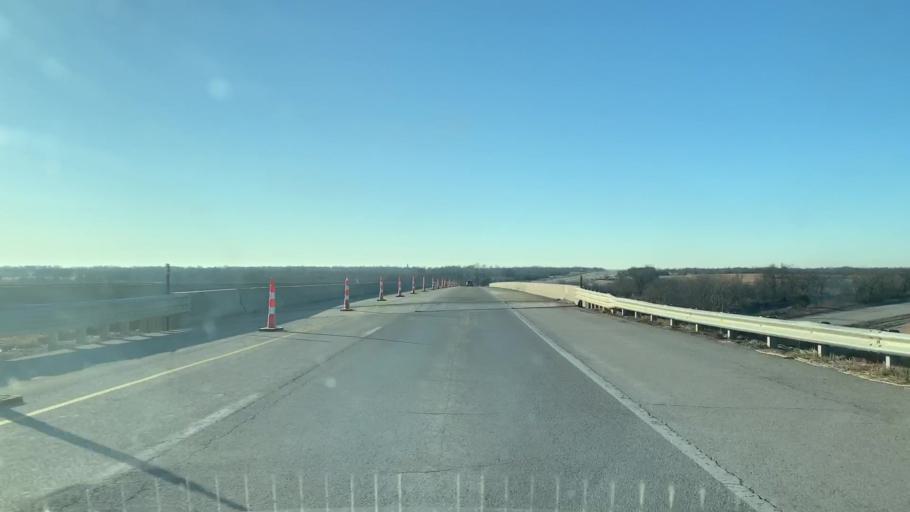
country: US
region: Kansas
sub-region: Bourbon County
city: Fort Scott
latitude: 37.7685
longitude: -94.7057
